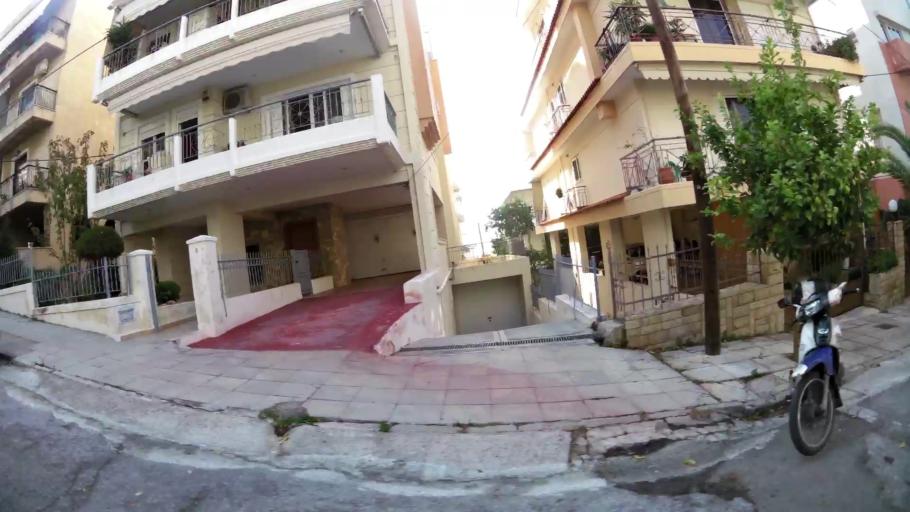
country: GR
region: Attica
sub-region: Nomarchia Athinas
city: Ilioupoli
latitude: 37.9254
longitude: 23.7627
